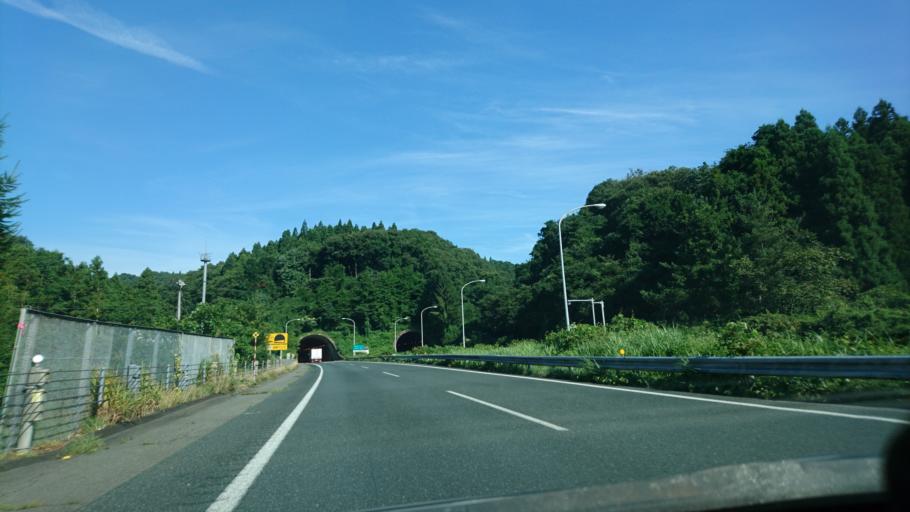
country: JP
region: Iwate
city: Ichinoseki
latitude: 38.9880
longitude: 141.1032
